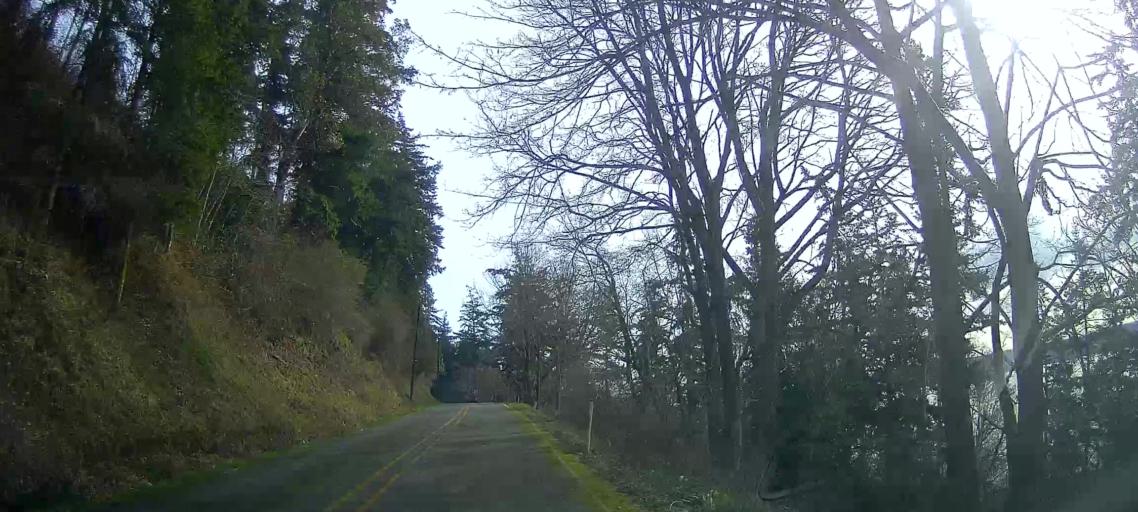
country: US
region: Washington
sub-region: Island County
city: Langley
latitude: 48.0656
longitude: -122.3858
